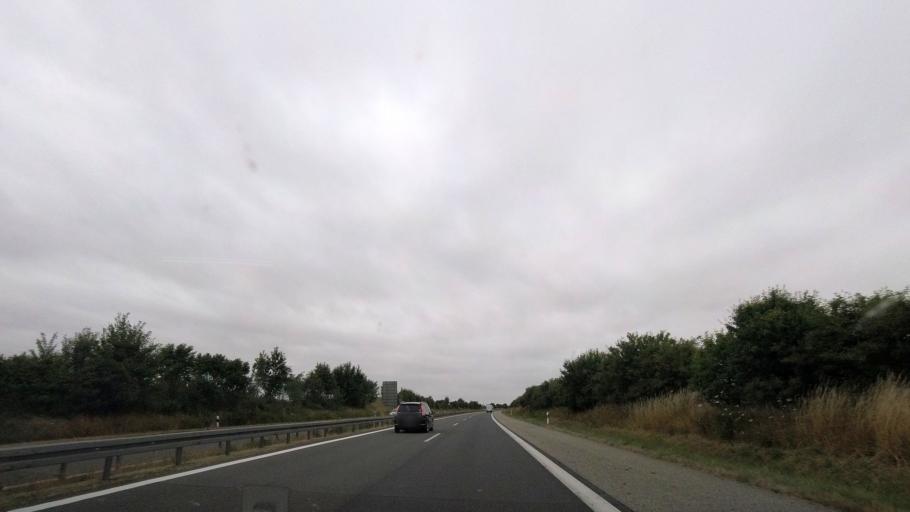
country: DE
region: Brandenburg
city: Gramzow
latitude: 53.2558
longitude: 14.0022
